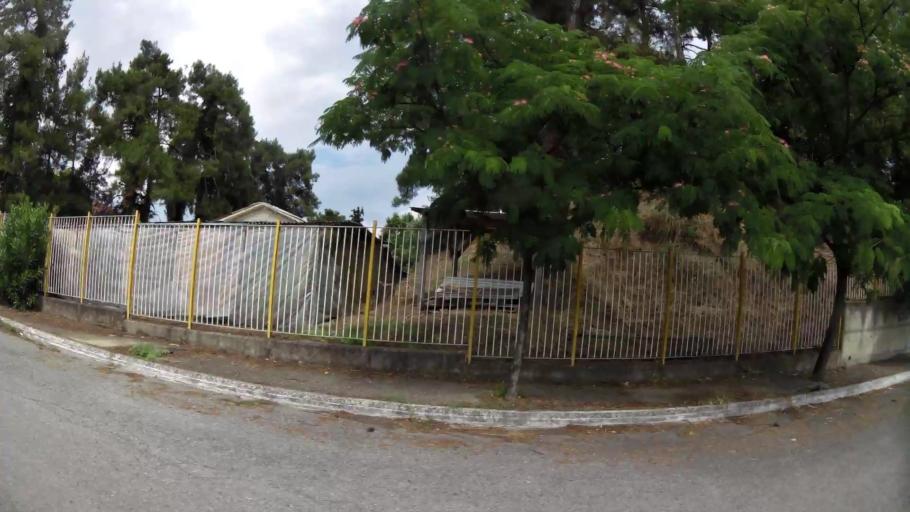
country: GR
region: Central Macedonia
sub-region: Nomos Pierias
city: Makrygialos
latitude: 40.4175
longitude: 22.6071
